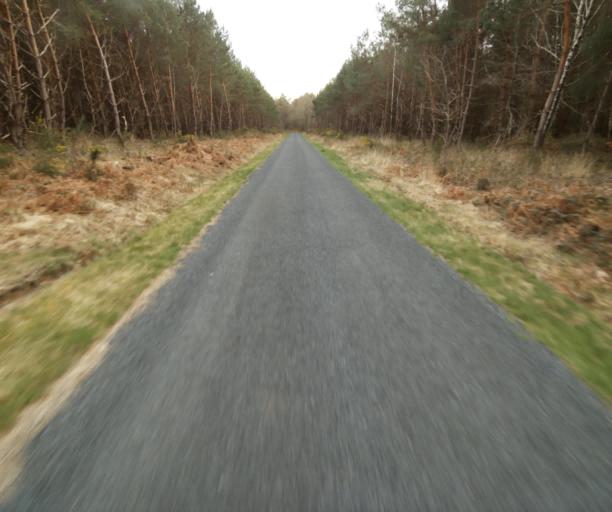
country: FR
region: Limousin
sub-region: Departement de la Correze
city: Saint-Privat
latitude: 45.1986
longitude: 2.0004
